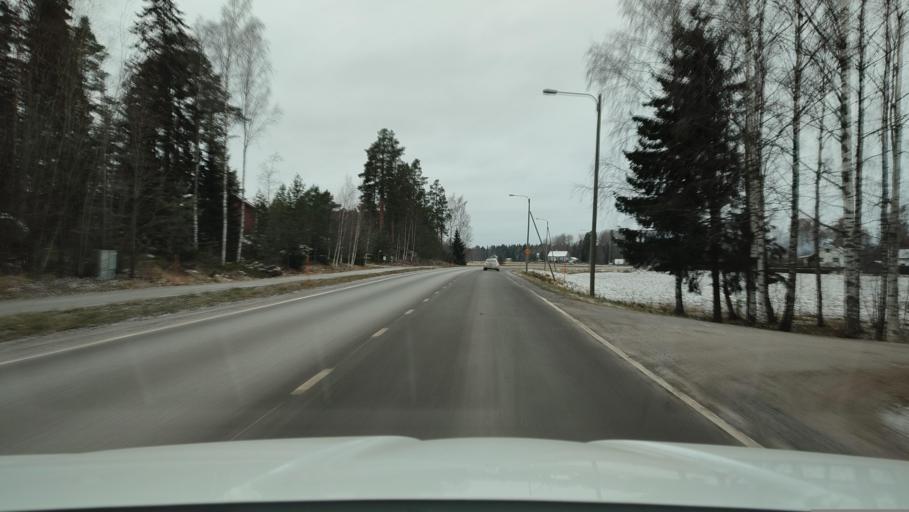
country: FI
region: Ostrobothnia
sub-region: Vaasa
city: Smedsby
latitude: 63.1278
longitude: 21.7008
